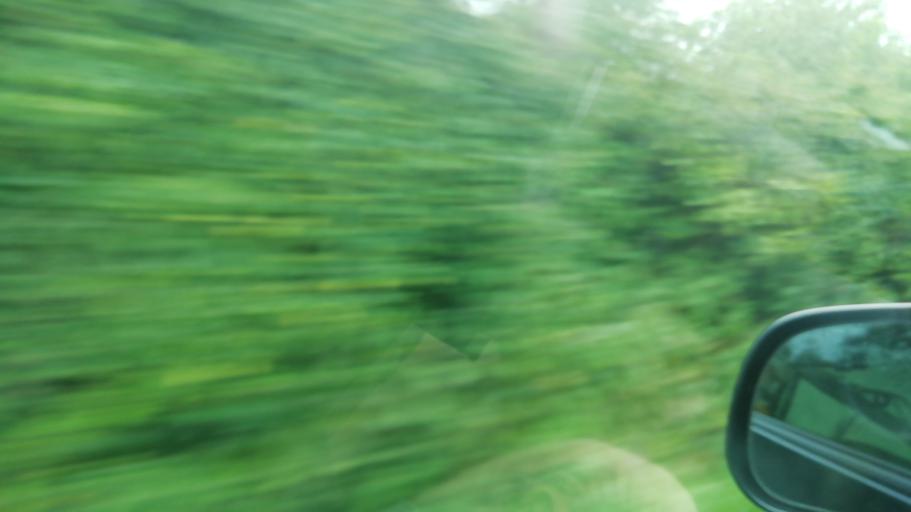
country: IE
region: Munster
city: Fethard
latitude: 52.5235
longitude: -7.6826
